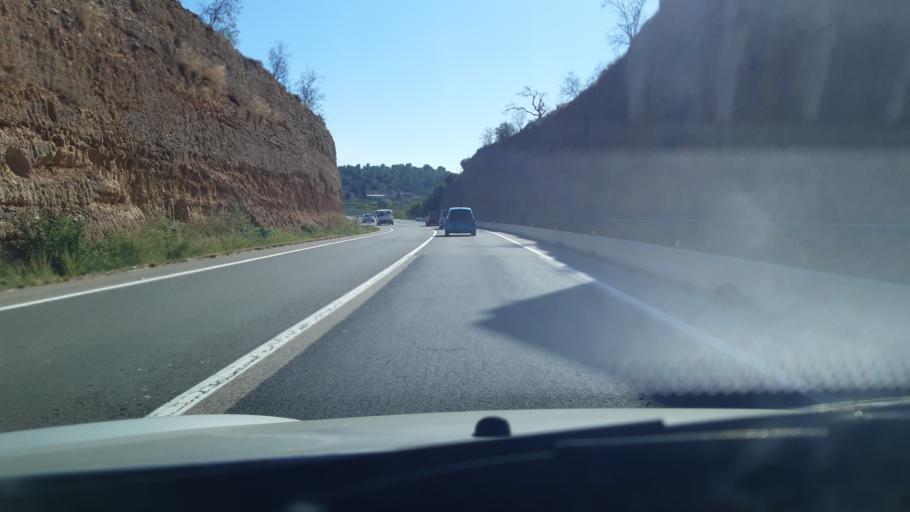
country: ES
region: Catalonia
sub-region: Provincia de Tarragona
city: Tivenys
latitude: 40.8865
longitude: 0.4918
